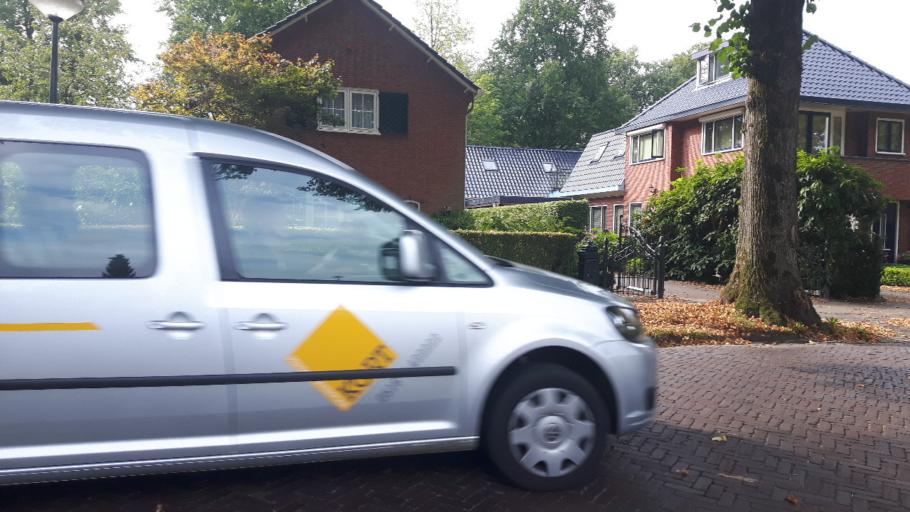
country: NL
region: Friesland
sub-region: Gemeente Heerenveen
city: Jubbega
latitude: 52.9908
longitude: 6.2892
